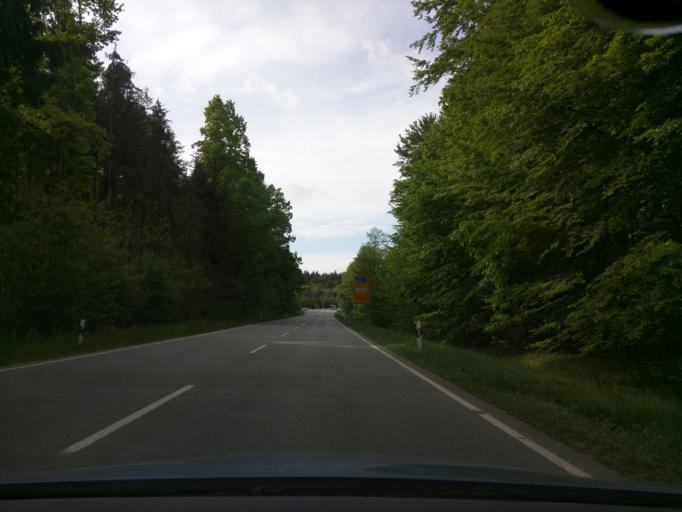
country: DE
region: Bavaria
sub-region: Lower Bavaria
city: Passau
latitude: 48.5439
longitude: 13.4066
